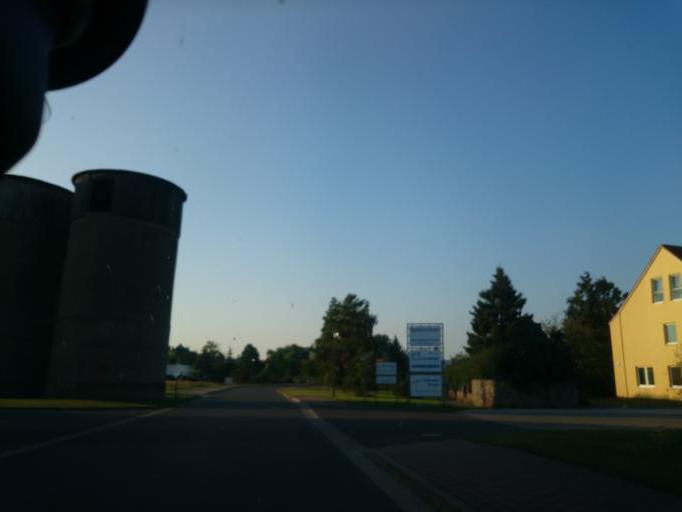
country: DE
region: Mecklenburg-Vorpommern
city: Saal
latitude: 54.3116
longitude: 12.4997
